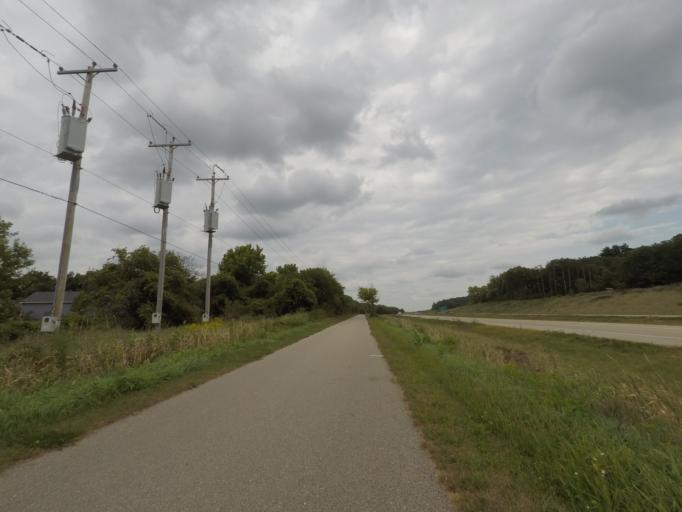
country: US
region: Wisconsin
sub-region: Jefferson County
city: Lake Koshkonong
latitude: 42.8734
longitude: -88.8891
